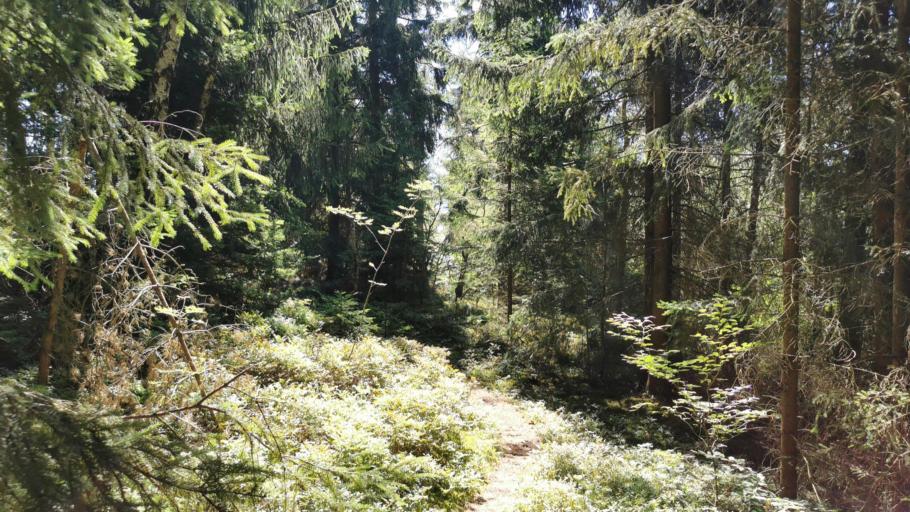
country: DE
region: Thuringia
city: Grafenthal
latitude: 50.5039
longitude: 11.3219
